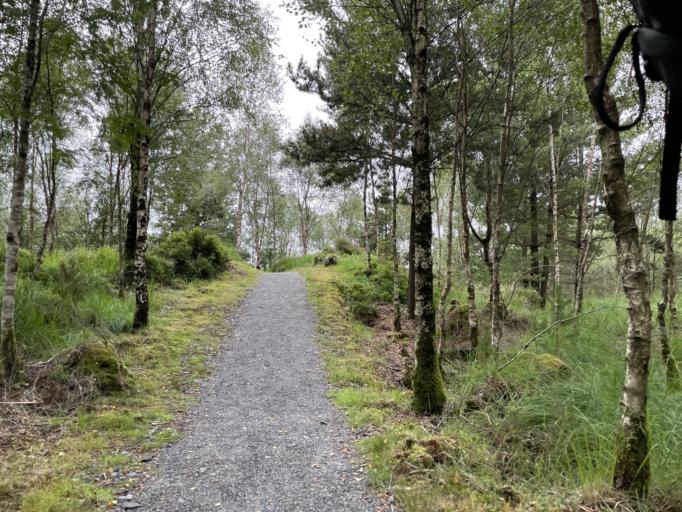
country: GB
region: Scotland
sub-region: Dumfries and Galloway
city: Newton Stewart
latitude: 55.0824
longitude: -4.5091
